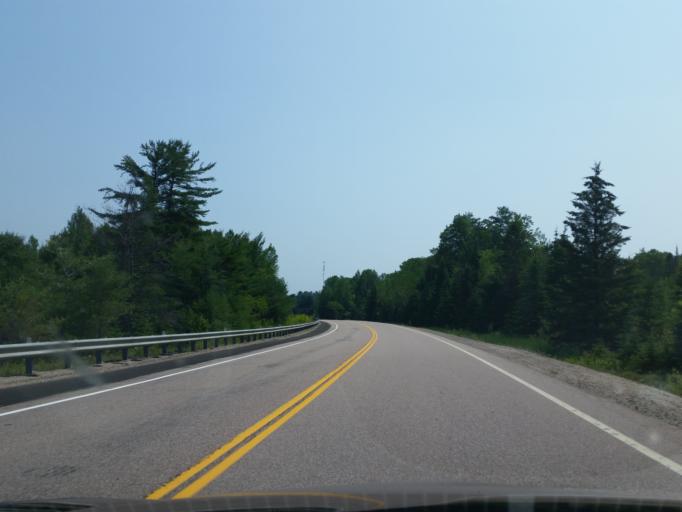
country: CA
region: Ontario
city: Deep River
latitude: 46.1690
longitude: -77.8110
